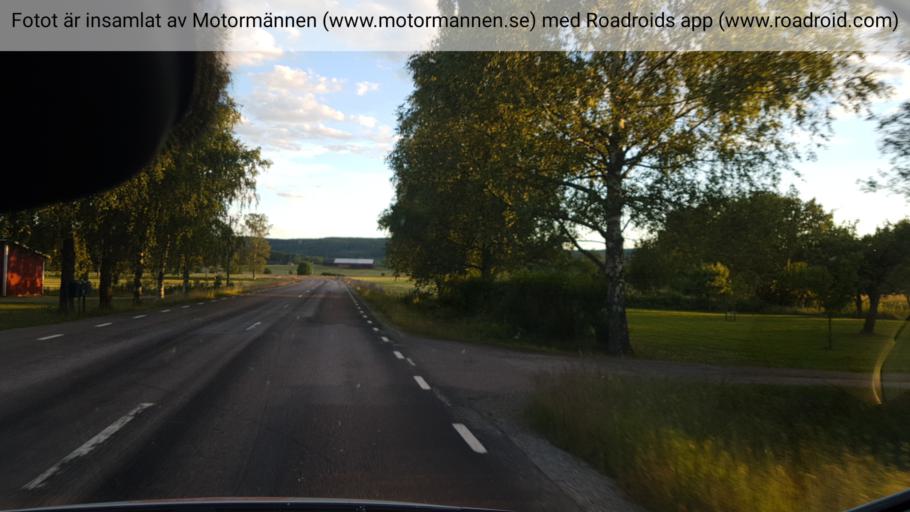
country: SE
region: Vaermland
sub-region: Sunne Kommun
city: Sunne
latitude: 59.7301
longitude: 13.1258
